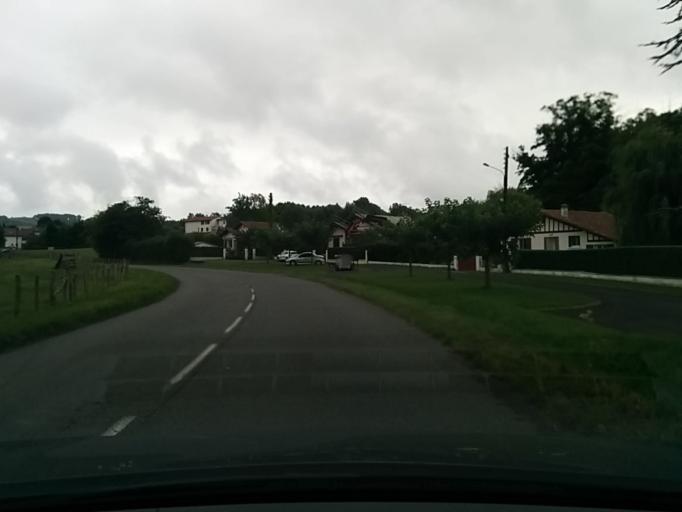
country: FR
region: Aquitaine
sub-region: Departement des Pyrenees-Atlantiques
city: Saint-Pee-sur-Nivelle
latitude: 43.3459
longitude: -1.5522
